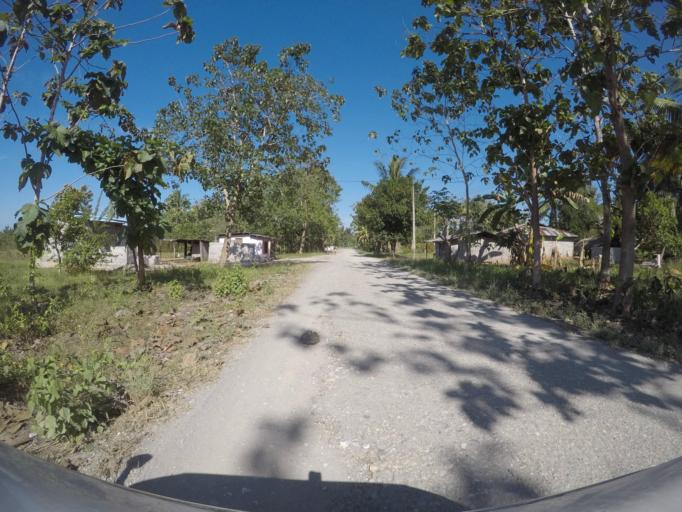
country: TL
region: Viqueque
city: Viqueque
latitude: -8.9338
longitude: 126.1287
